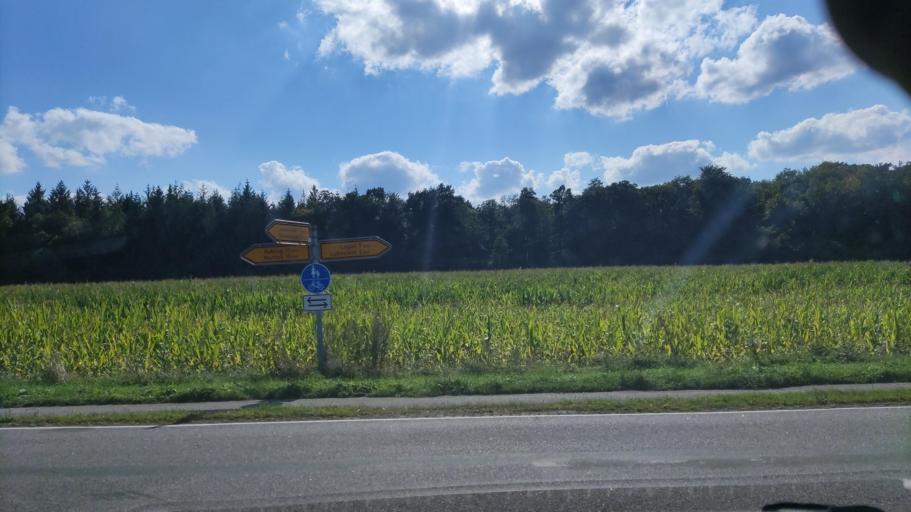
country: DE
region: Schleswig-Holstein
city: Oldenhutten
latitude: 54.1718
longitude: 9.7365
